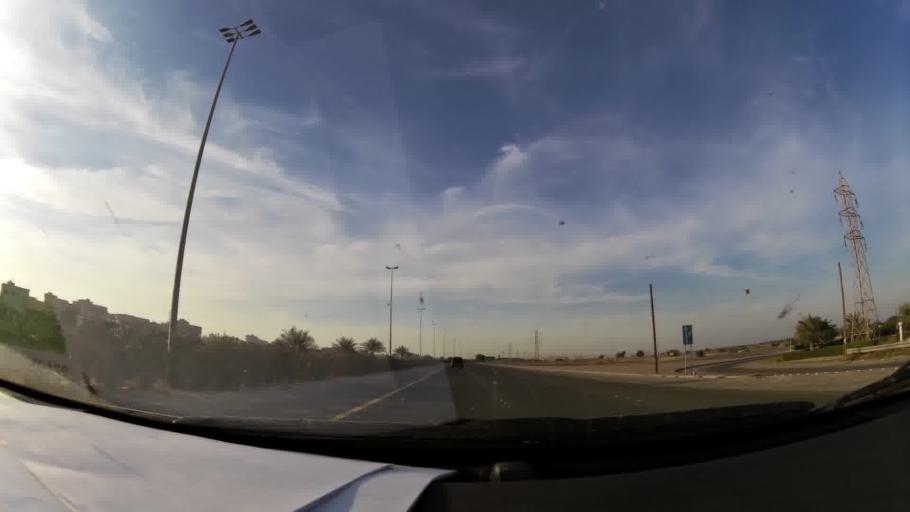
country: KW
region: Al Ahmadi
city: Al Fahahil
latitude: 28.9575
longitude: 48.1702
